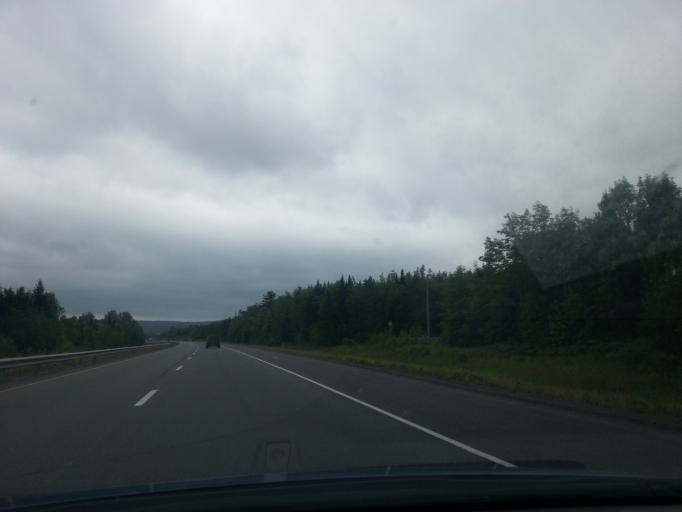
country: US
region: Maine
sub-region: Aroostook County
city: Houlton
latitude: 46.0566
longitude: -67.5681
